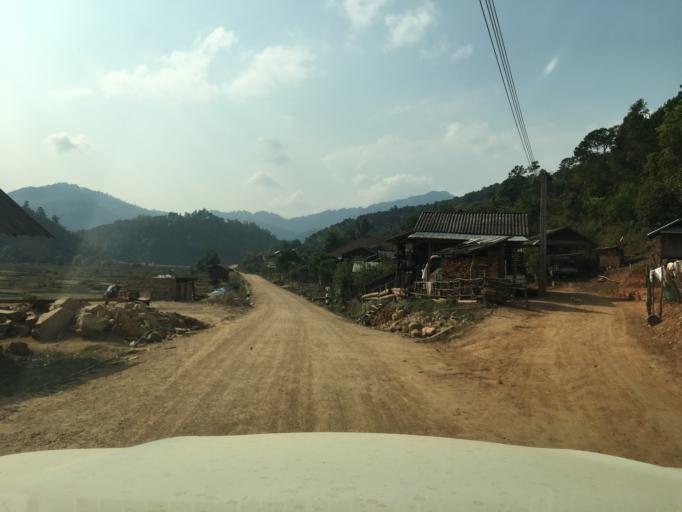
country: LA
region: Houaphan
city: Huameung
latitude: 20.2034
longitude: 103.8404
